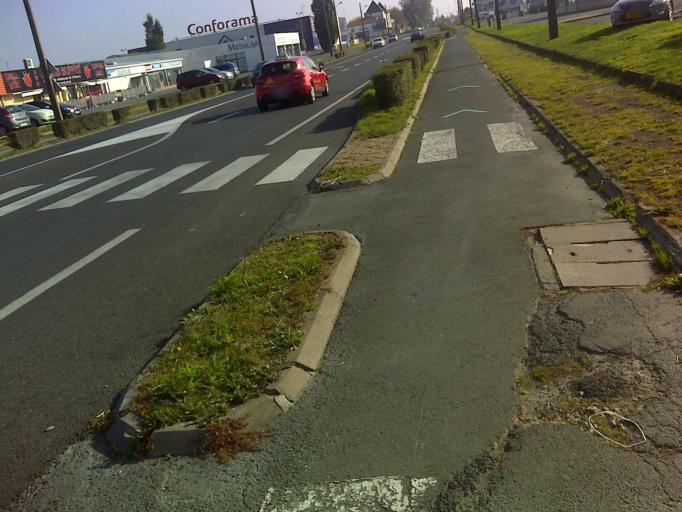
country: FR
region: Poitou-Charentes
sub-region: Departement de la Charente-Maritime
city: Breuil-Magne
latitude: 45.9505
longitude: -0.9357
